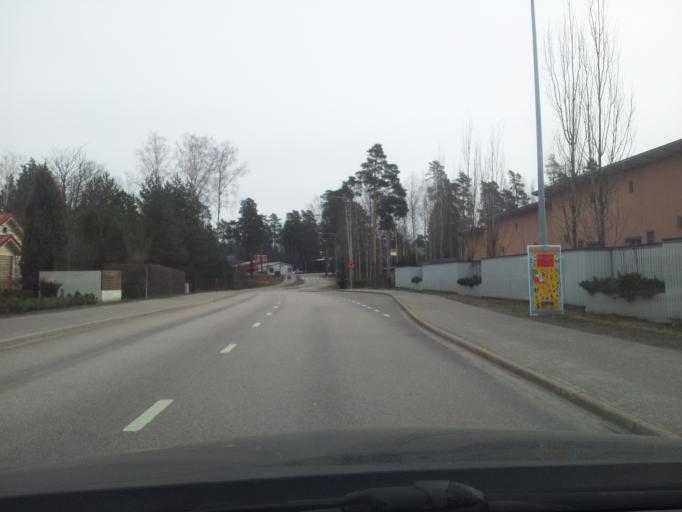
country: FI
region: Uusimaa
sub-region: Helsinki
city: Kilo
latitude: 60.1959
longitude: 24.7942
